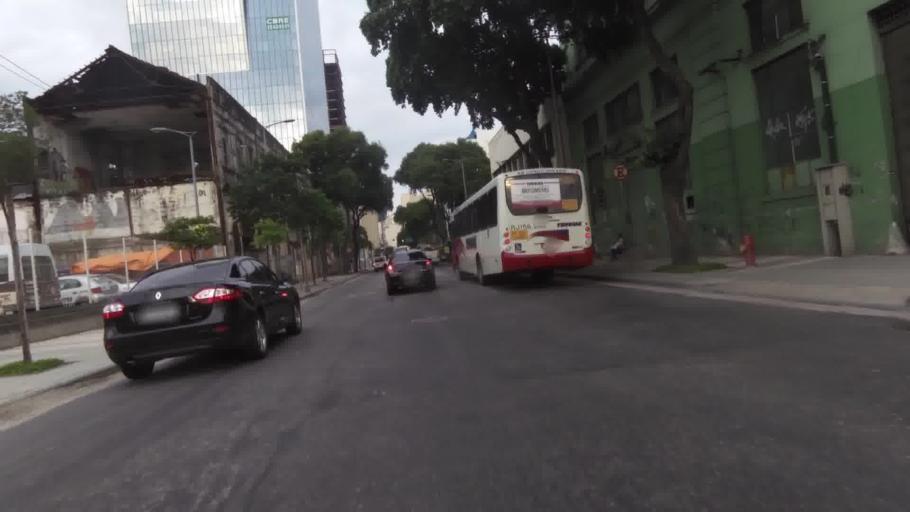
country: BR
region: Rio de Janeiro
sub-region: Rio De Janeiro
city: Rio de Janeiro
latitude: -22.8951
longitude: -43.1886
